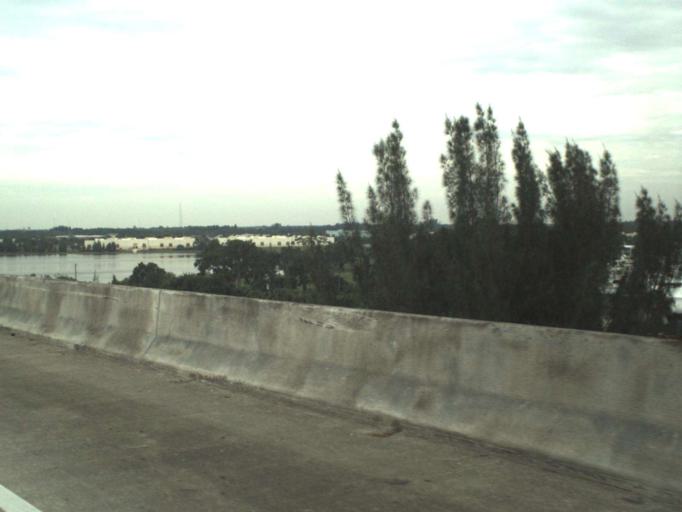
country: US
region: Florida
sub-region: Martin County
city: Palm City
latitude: 27.1197
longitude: -80.2702
